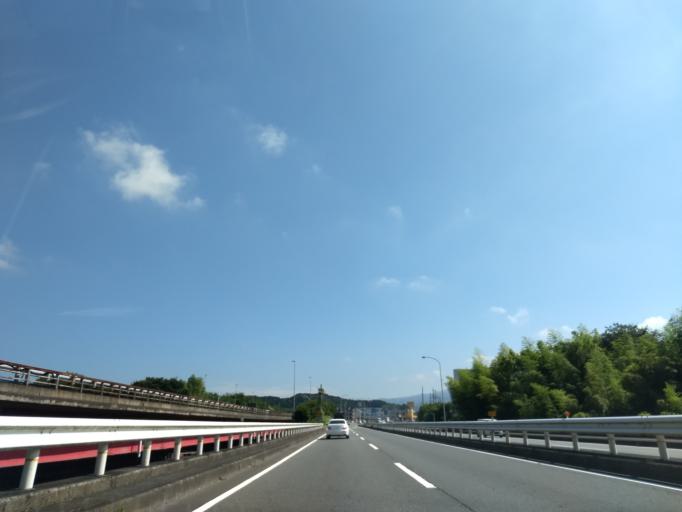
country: JP
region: Shizuoka
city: Mishima
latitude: 35.1847
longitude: 138.9013
